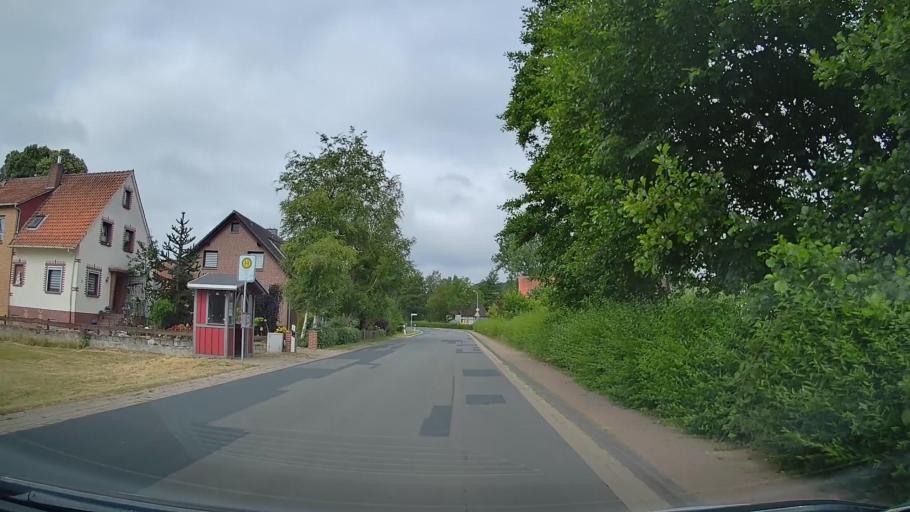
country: DE
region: Lower Saxony
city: Aerzen
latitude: 52.0427
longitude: 9.1955
